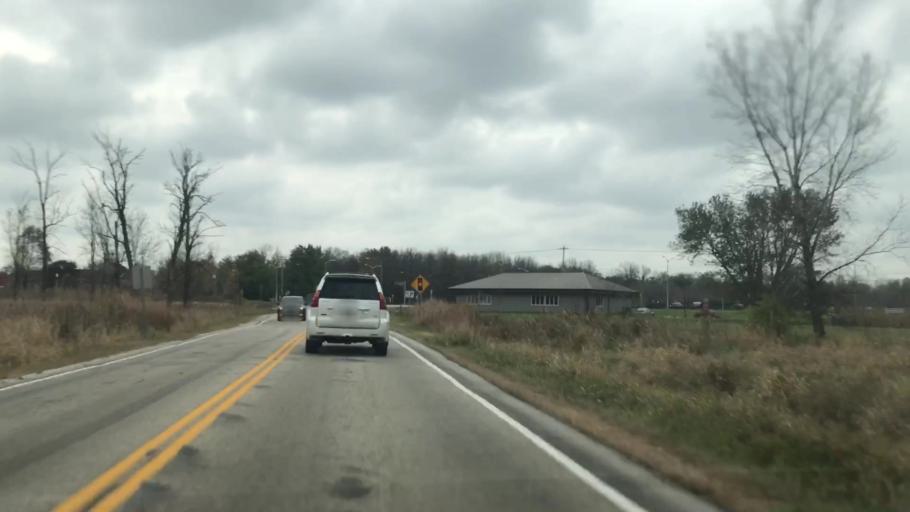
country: US
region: Wisconsin
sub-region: Waukesha County
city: Menomonee Falls
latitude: 43.1981
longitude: -88.1427
